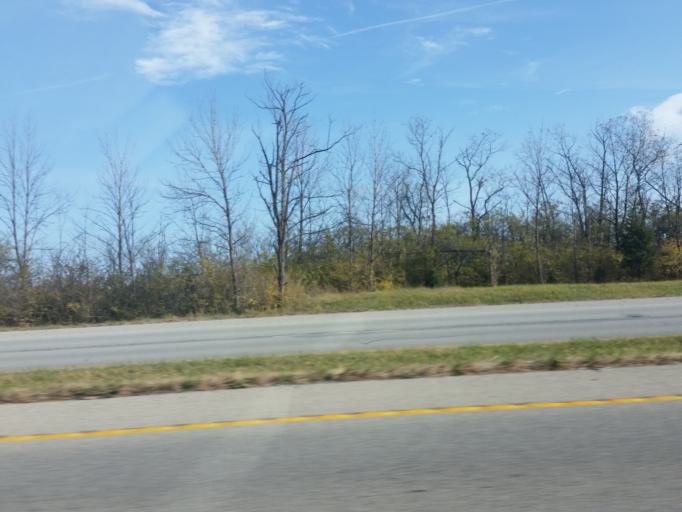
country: US
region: Ohio
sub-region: Hamilton County
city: Dry Ridge
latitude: 39.2687
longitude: -84.6030
